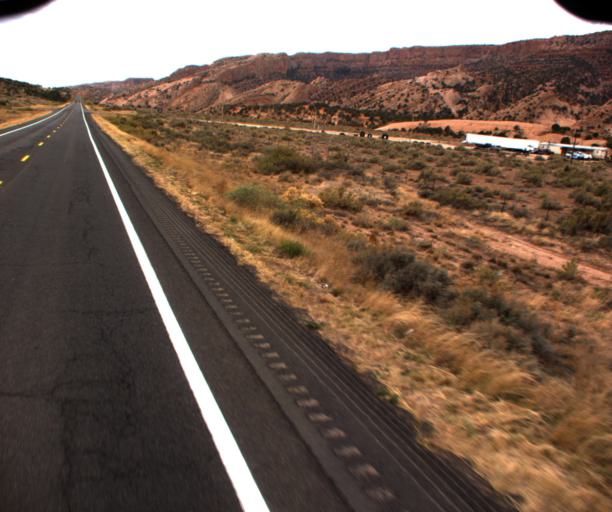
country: US
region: Arizona
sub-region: Navajo County
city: Kayenta
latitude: 36.6705
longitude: -110.4039
